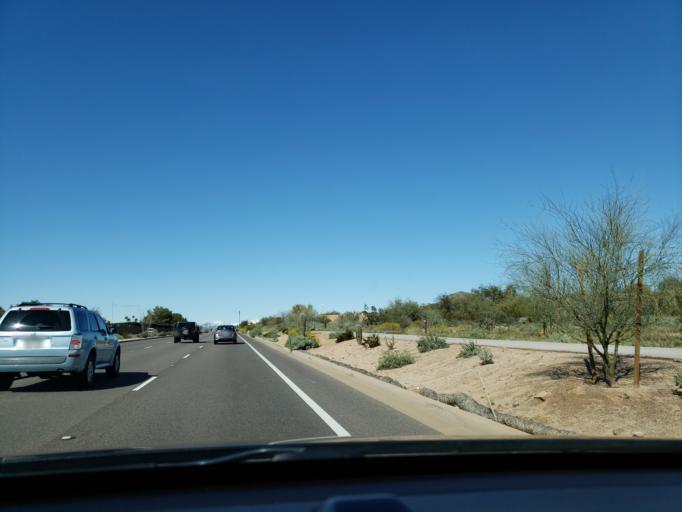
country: US
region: Arizona
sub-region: Maricopa County
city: Carefree
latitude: 33.6903
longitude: -111.8904
